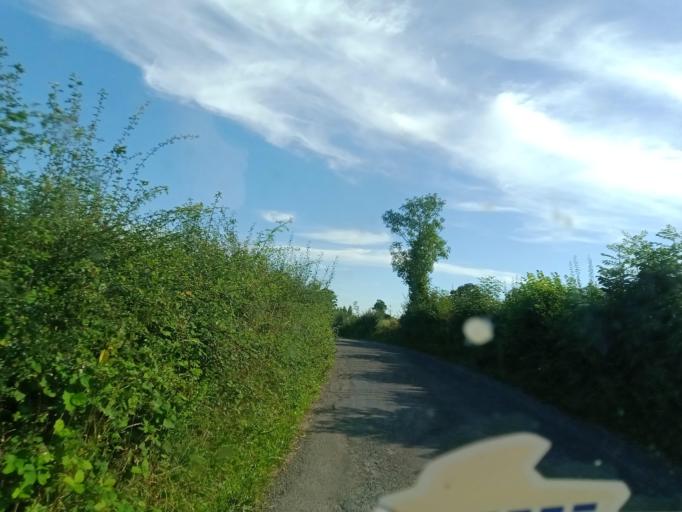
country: IE
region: Leinster
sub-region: Kilkenny
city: Ballyragget
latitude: 52.7672
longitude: -7.3920
